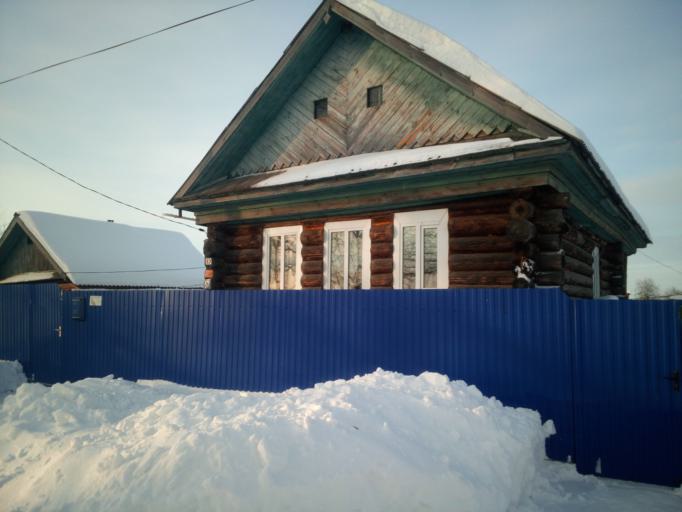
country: RU
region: Bashkortostan
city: Amzya
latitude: 56.1673
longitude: 54.3811
